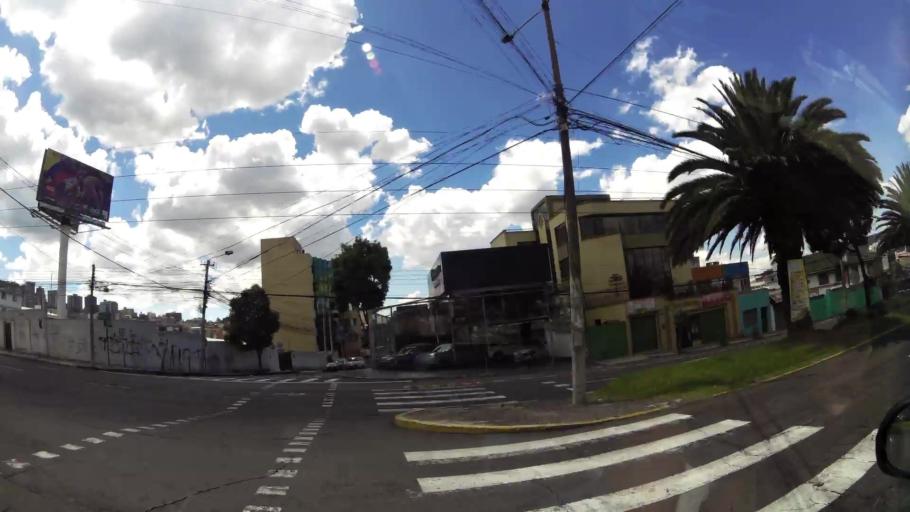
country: EC
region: Pichincha
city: Quito
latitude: -0.1749
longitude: -78.4916
